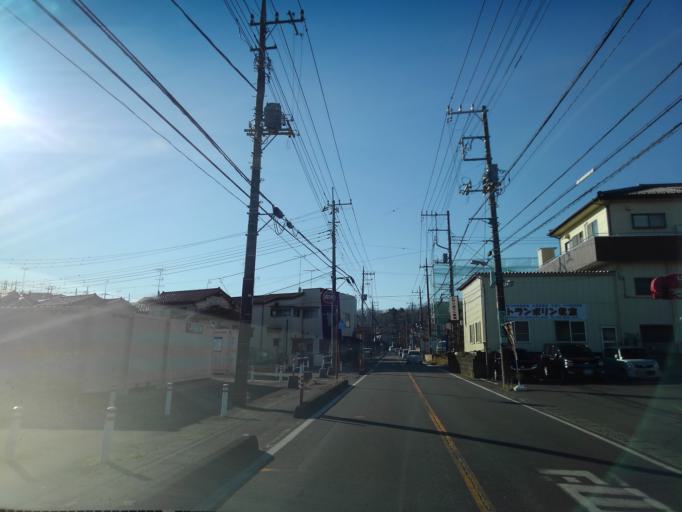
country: JP
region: Saitama
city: Tokorozawa
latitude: 35.7849
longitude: 139.4266
